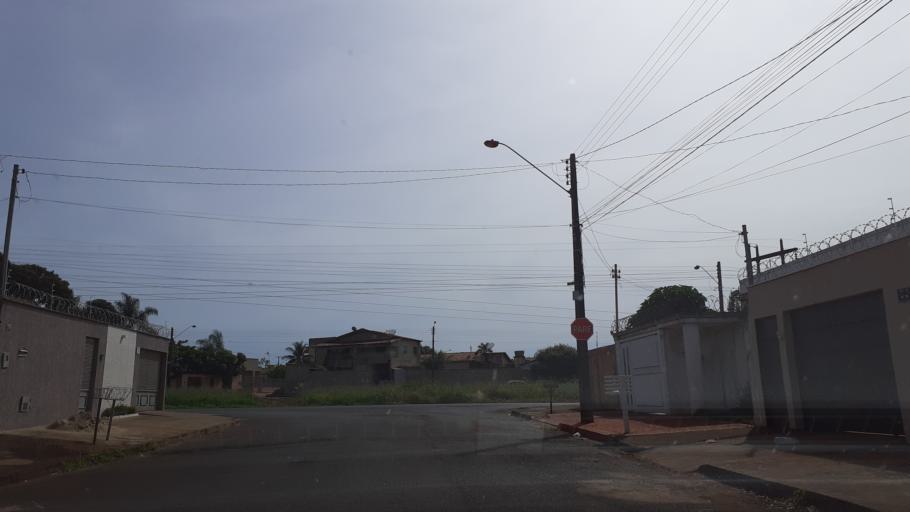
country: BR
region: Goias
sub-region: Itumbiara
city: Itumbiara
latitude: -18.4198
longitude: -49.2413
